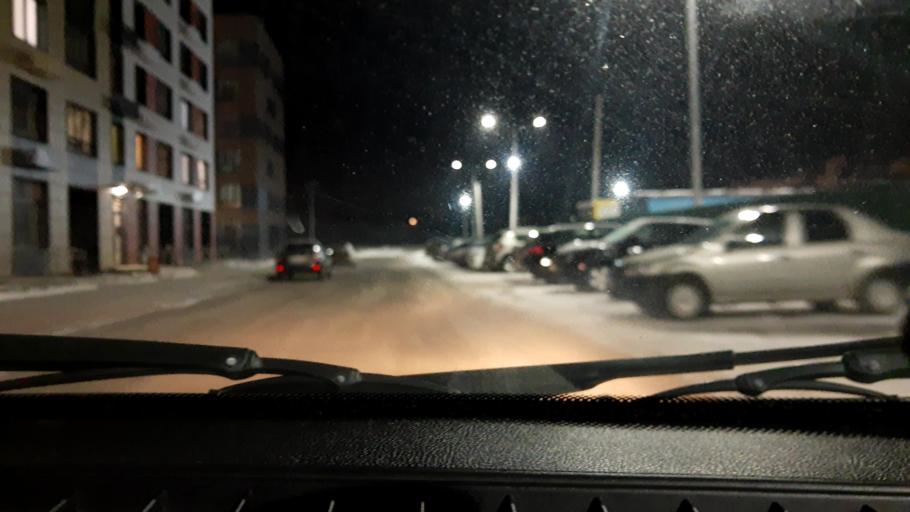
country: RU
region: Bashkortostan
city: Ufa
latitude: 54.6733
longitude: 55.9197
